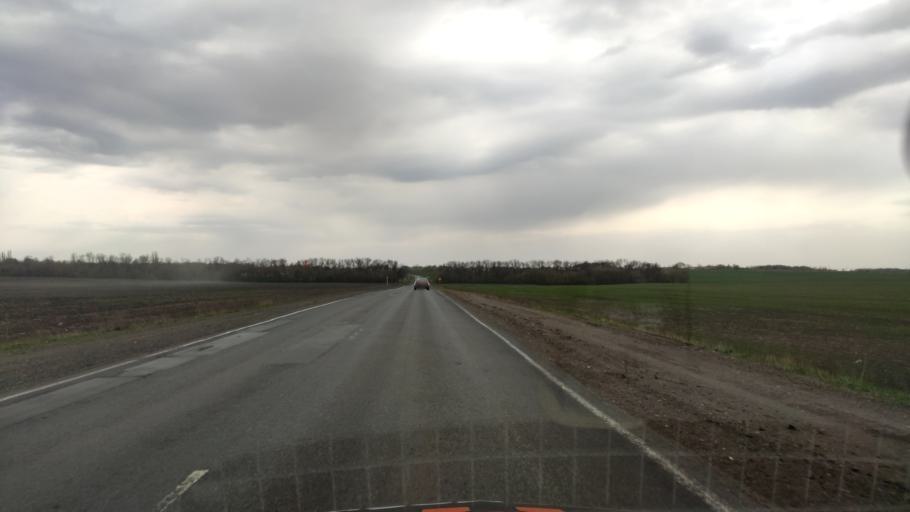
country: RU
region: Kursk
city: Gorshechnoye
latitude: 51.5443
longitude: 38.0264
